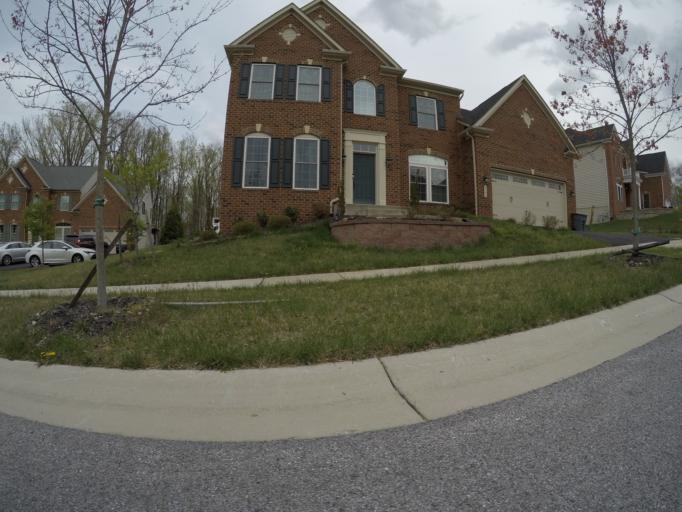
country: US
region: Maryland
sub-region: Howard County
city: Ellicott City
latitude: 39.2574
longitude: -76.7869
